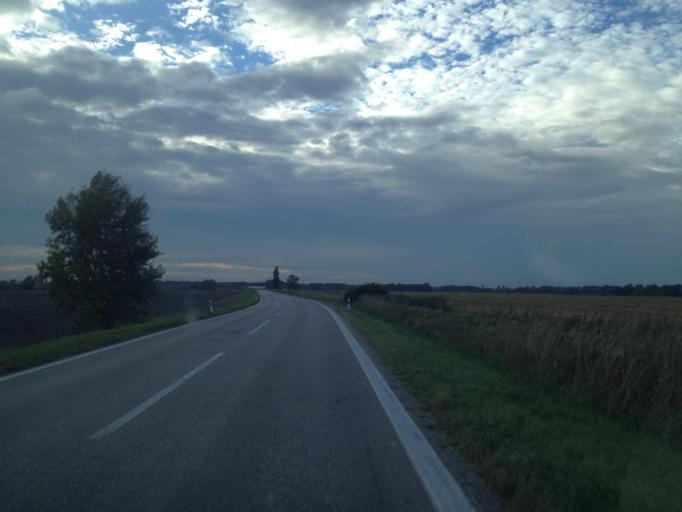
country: SK
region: Nitriansky
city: Komarno
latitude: 47.7623
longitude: 18.1824
